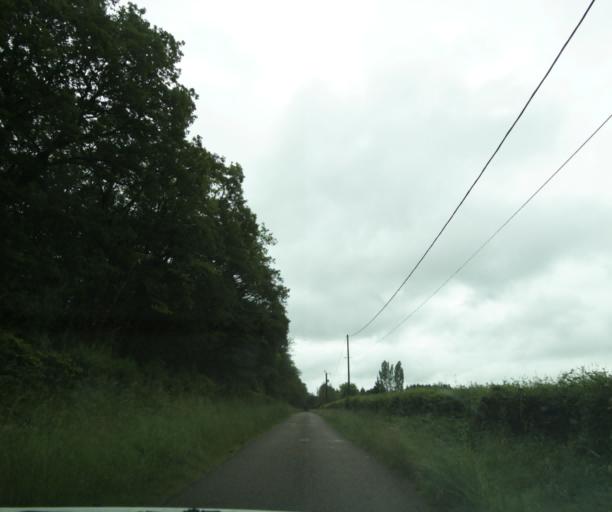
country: FR
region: Bourgogne
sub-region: Departement de Saone-et-Loire
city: Charolles
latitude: 46.5049
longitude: 4.2909
